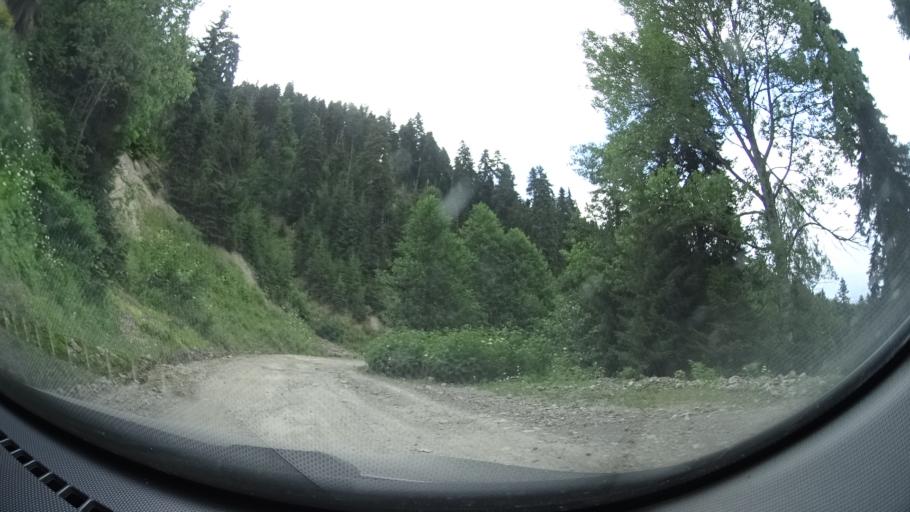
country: GE
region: Samtskhe-Javakheti
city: Adigeni
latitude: 41.6351
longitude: 42.5790
